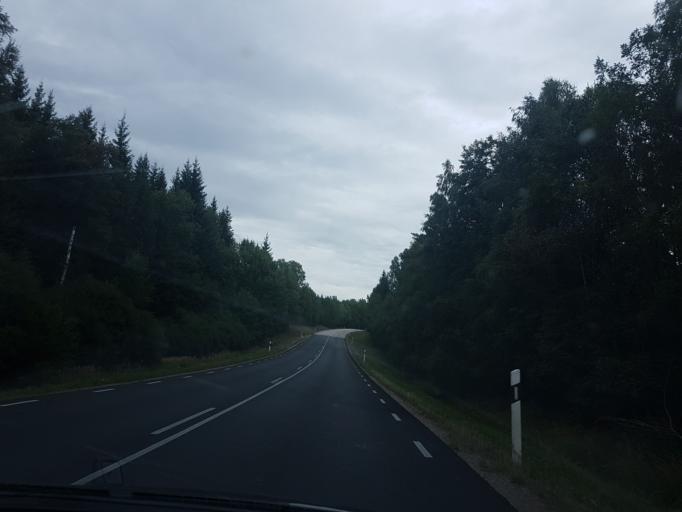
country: SE
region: Joenkoeping
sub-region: Vetlanda Kommun
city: Vetlanda
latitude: 57.3669
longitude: 15.1042
